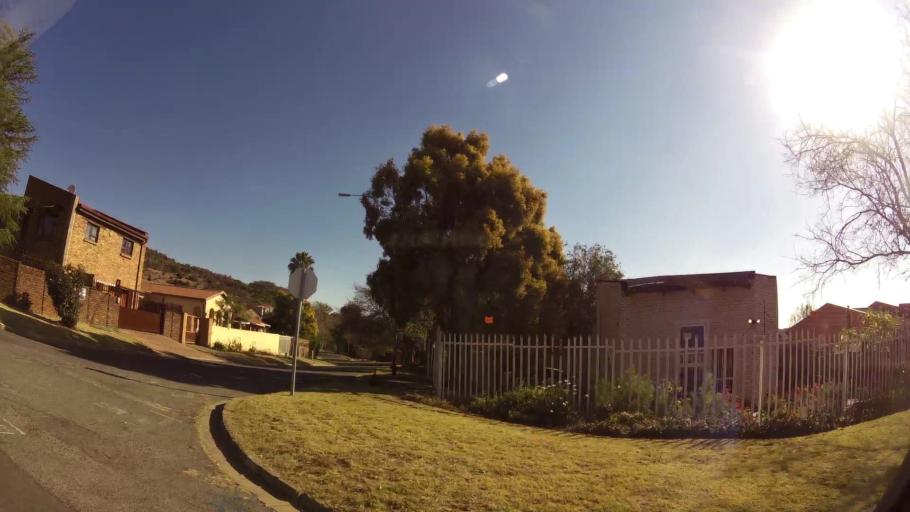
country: ZA
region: Gauteng
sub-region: City of Johannesburg Metropolitan Municipality
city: Johannesburg
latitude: -26.2777
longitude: 28.0275
